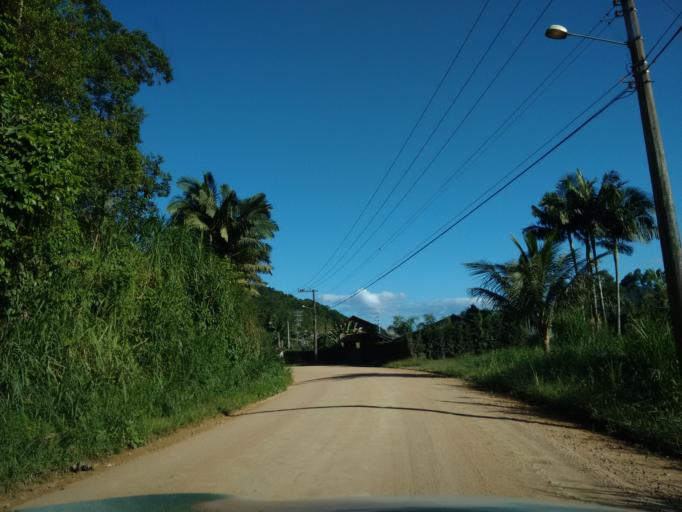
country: BR
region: Santa Catarina
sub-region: Pomerode
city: Pomerode
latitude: -26.7540
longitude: -49.1678
